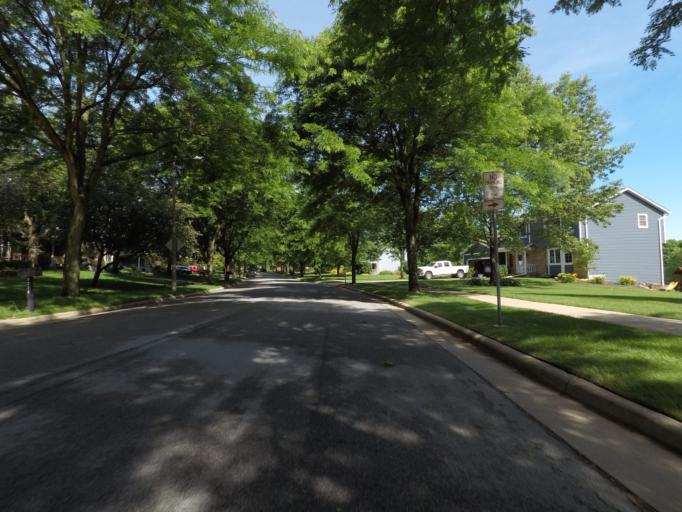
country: US
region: Wisconsin
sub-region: Dane County
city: Middleton
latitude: 43.0831
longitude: -89.5109
